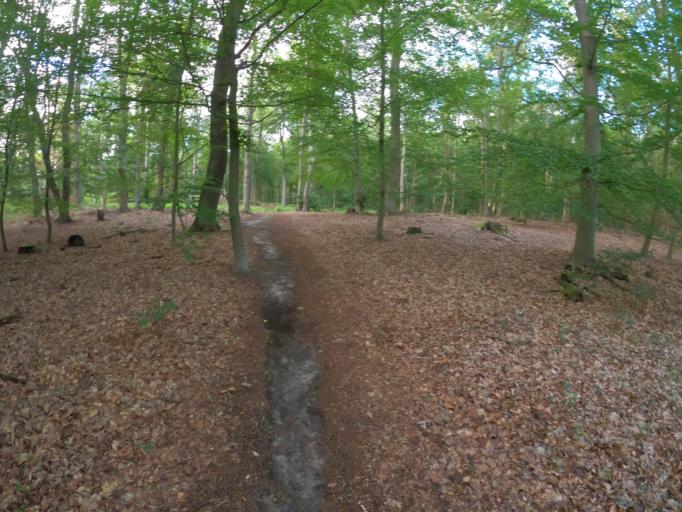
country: DE
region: Brandenburg
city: Angermunde
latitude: 53.0240
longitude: 13.9116
